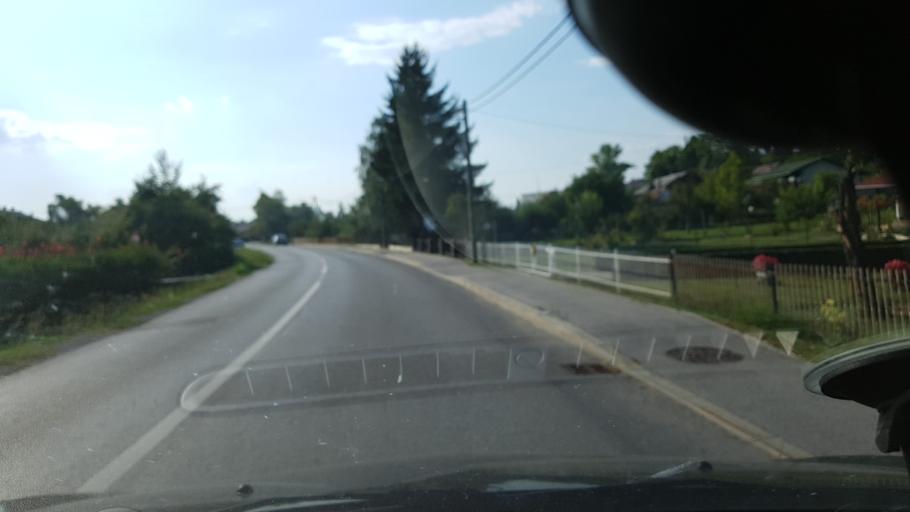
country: HR
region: Zagrebacka
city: Bregana
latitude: 45.8866
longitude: 15.6999
